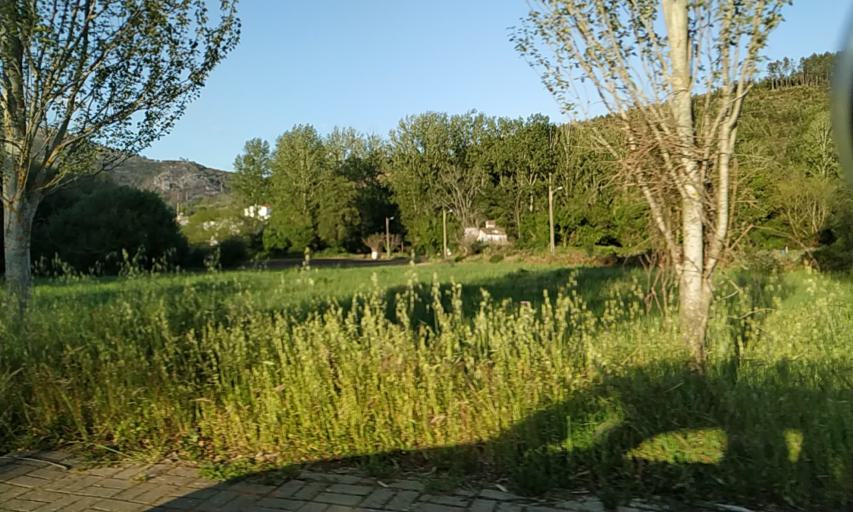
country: PT
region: Portalegre
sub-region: Marvao
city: Marvao
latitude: 39.3798
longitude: -7.3882
